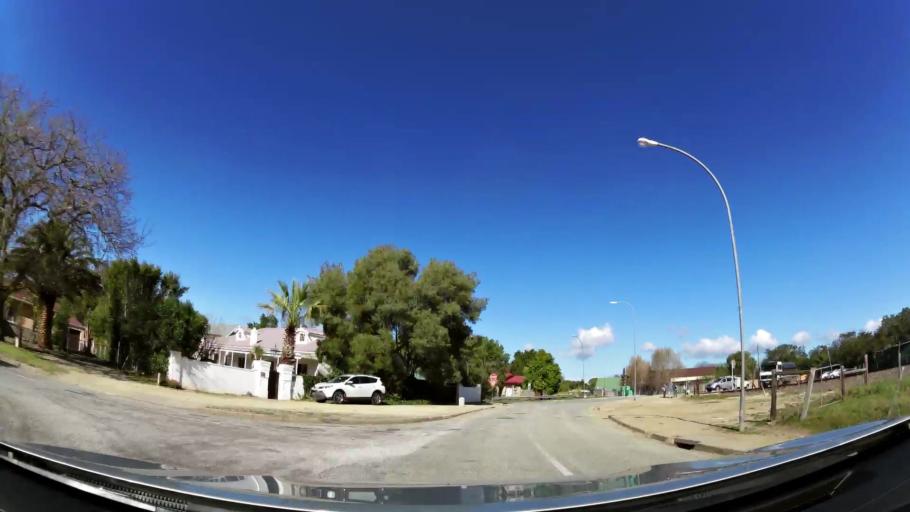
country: ZA
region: Western Cape
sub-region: Eden District Municipality
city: George
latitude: -33.9462
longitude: 22.4656
